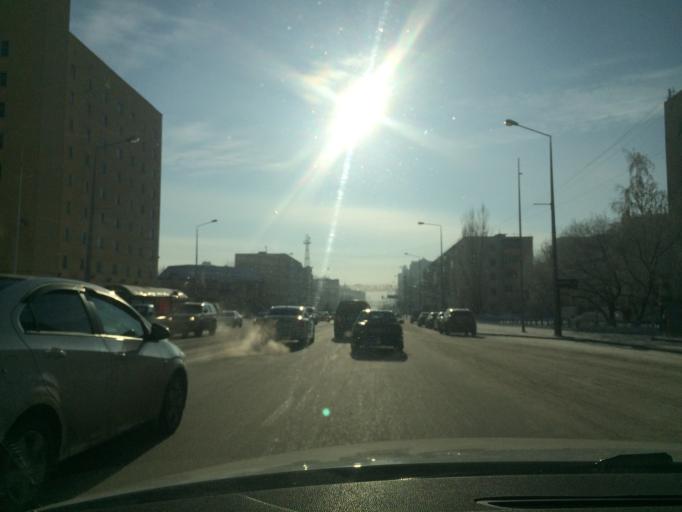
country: KZ
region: Astana Qalasy
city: Astana
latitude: 51.1744
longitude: 71.4065
